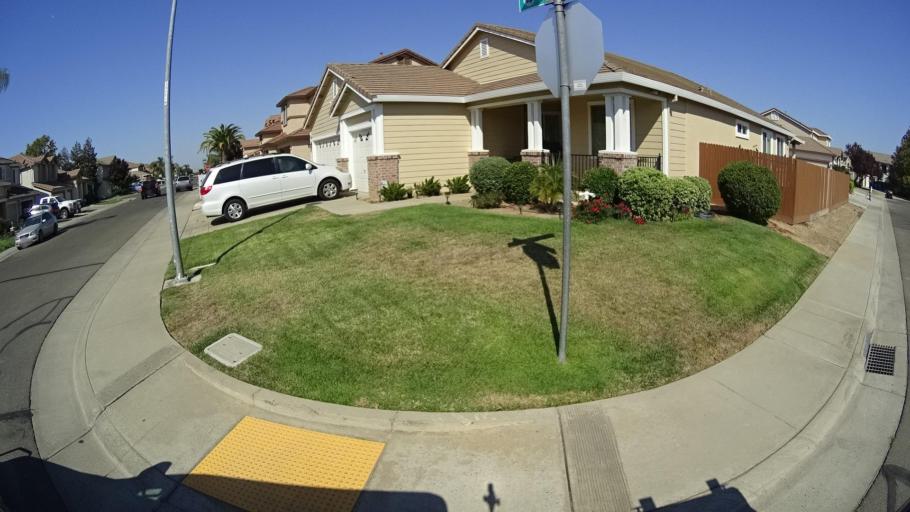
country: US
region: California
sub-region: Sacramento County
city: Laguna
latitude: 38.4457
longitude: -121.3963
